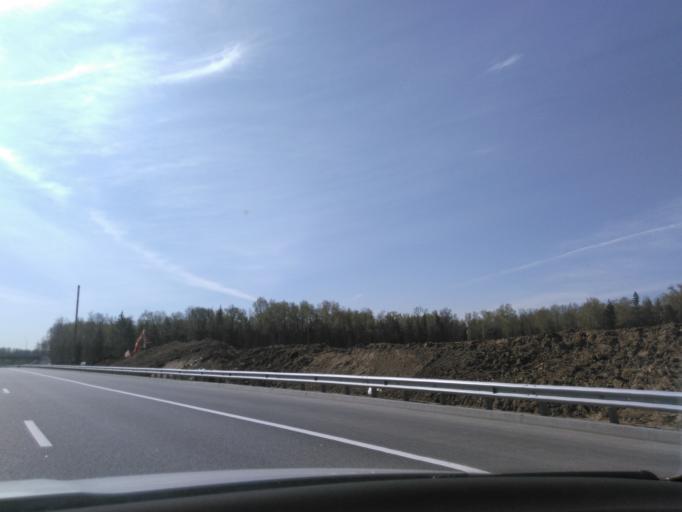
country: RU
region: Moscow
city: Khimki
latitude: 55.9478
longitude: 37.4400
